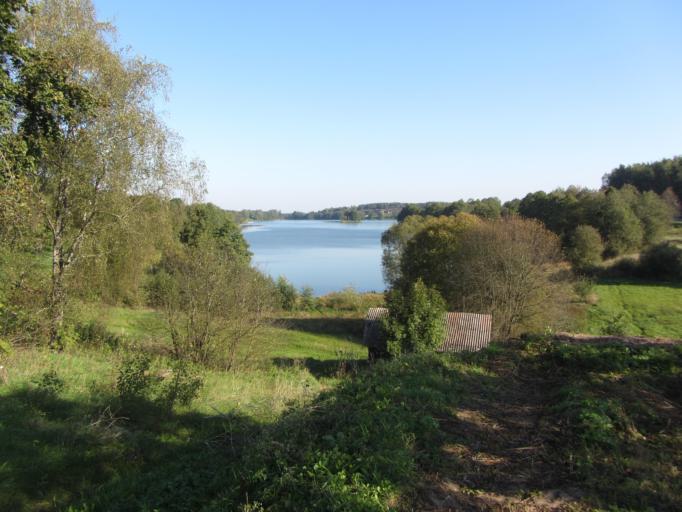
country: LT
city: Trakai
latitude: 54.6151
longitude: 24.9249
